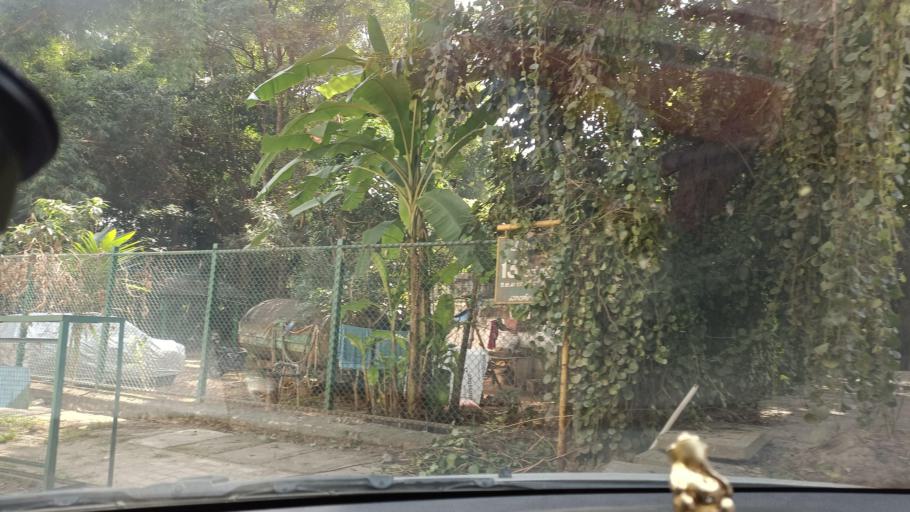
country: IN
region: Karnataka
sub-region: Bangalore Urban
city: Bangalore
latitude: 12.9082
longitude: 77.6137
